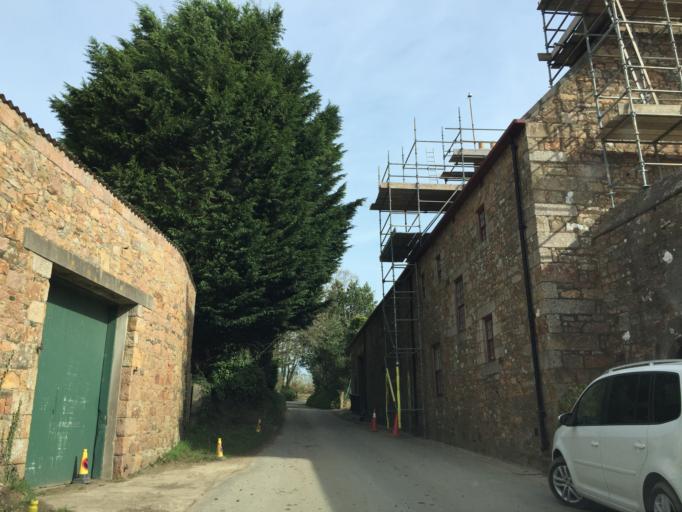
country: JE
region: St Helier
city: Saint Helier
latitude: 49.2241
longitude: -2.1361
